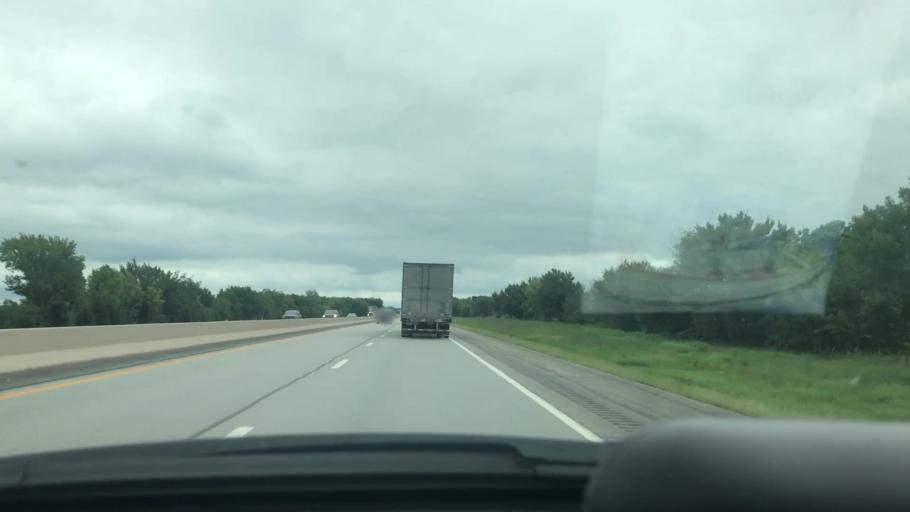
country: US
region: Oklahoma
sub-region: Ottawa County
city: Commerce
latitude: 36.8999
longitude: -94.8129
